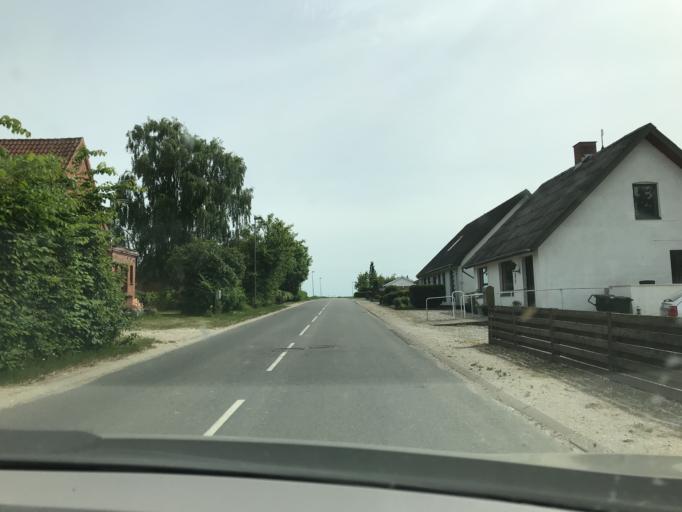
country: DK
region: Central Jutland
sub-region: Norddjurs Kommune
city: Allingabro
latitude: 56.5492
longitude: 10.2997
